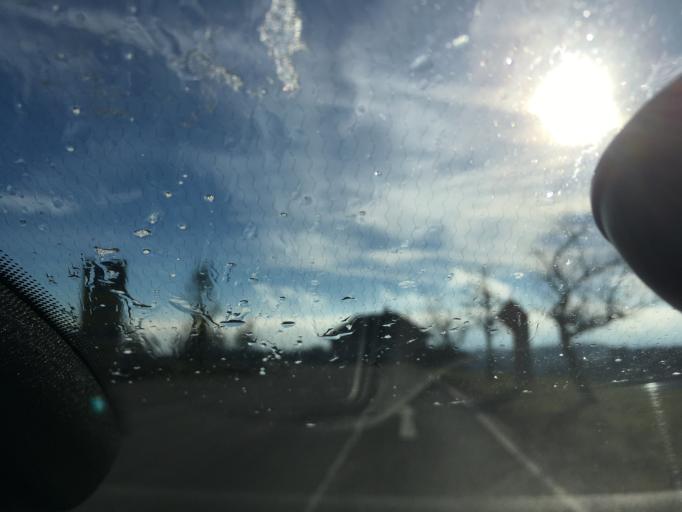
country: DE
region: Baden-Wuerttemberg
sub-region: Freiburg Region
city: Gorwihl
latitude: 47.6373
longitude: 8.0821
